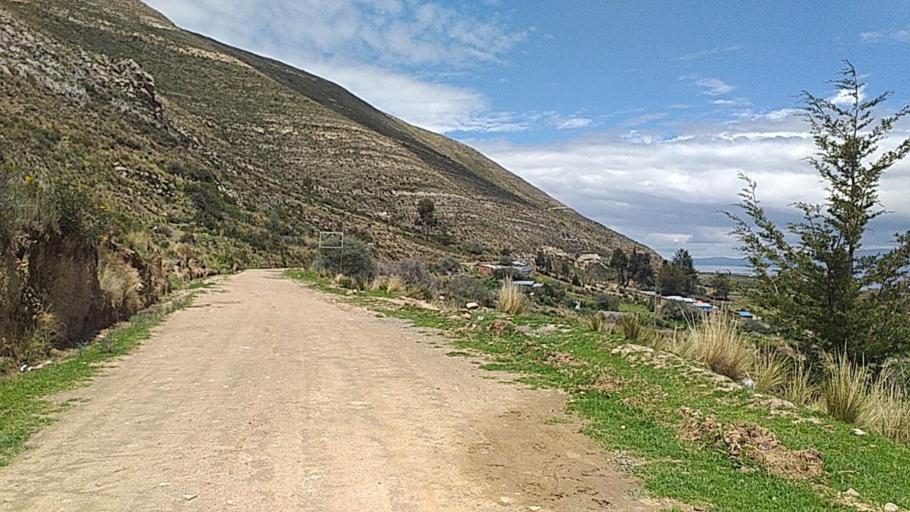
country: BO
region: La Paz
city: Huatajata
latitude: -16.3217
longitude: -68.6667
